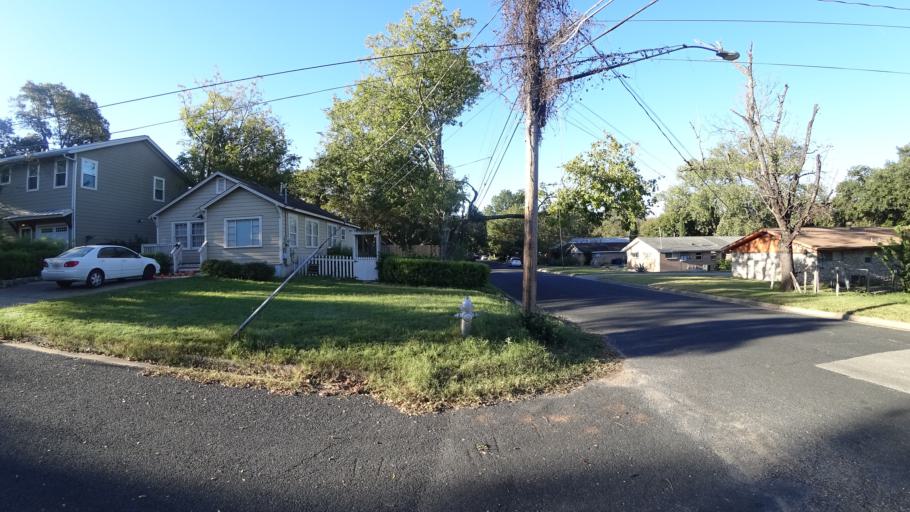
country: US
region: Texas
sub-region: Travis County
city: Austin
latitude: 30.3143
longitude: -97.7237
